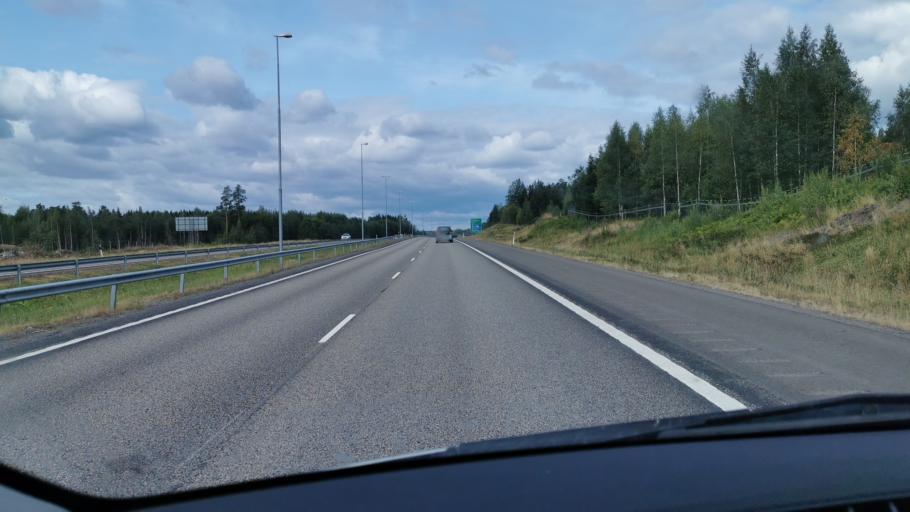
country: FI
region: Uusimaa
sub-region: Loviisa
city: Perna
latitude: 60.4908
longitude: 25.9920
